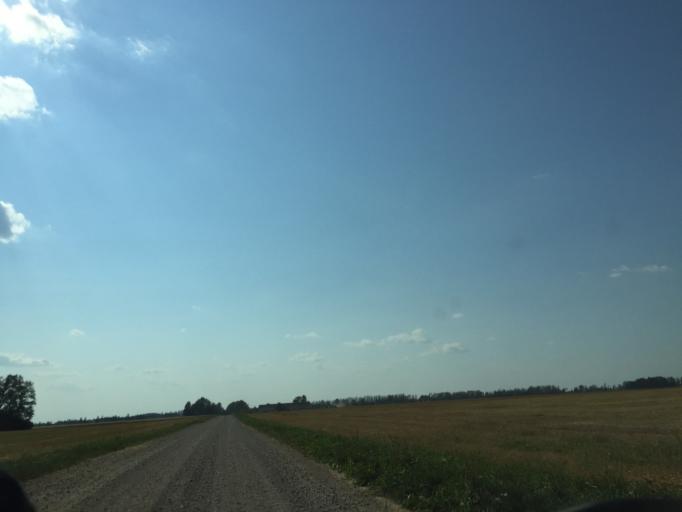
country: LV
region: Jelgava
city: Jelgava
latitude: 56.4548
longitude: 23.7170
